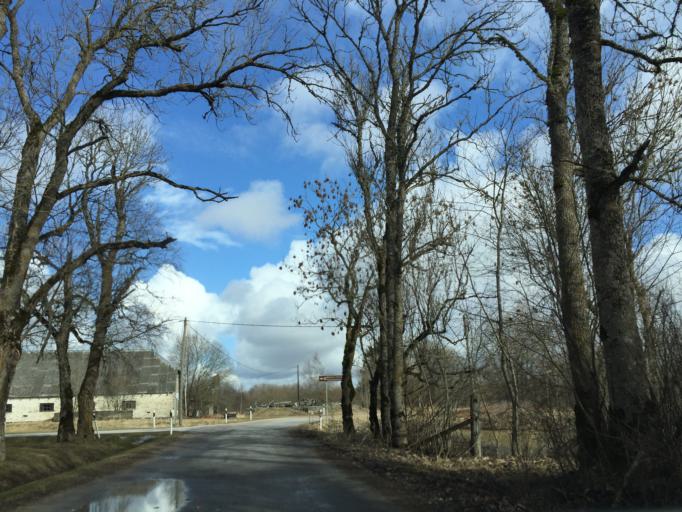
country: EE
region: Laeaene
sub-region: Lihula vald
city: Lihula
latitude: 58.7140
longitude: 23.8169
